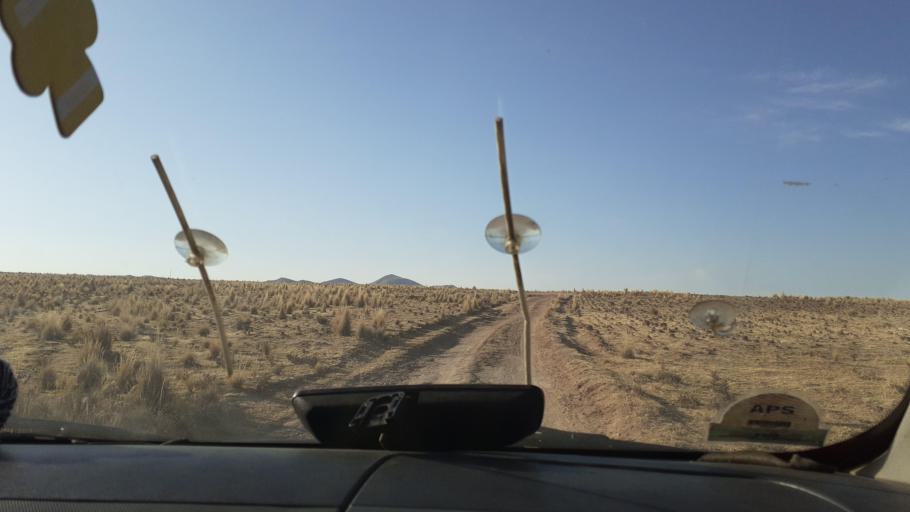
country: BO
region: La Paz
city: Tiahuanaco
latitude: -16.9890
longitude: -68.7328
